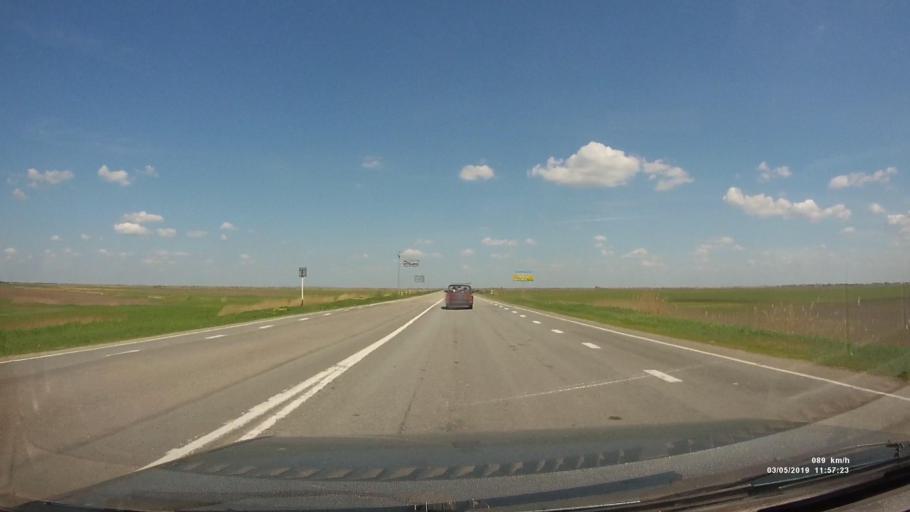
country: RU
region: Rostov
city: Bagayevskaya
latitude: 47.2059
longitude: 40.3093
